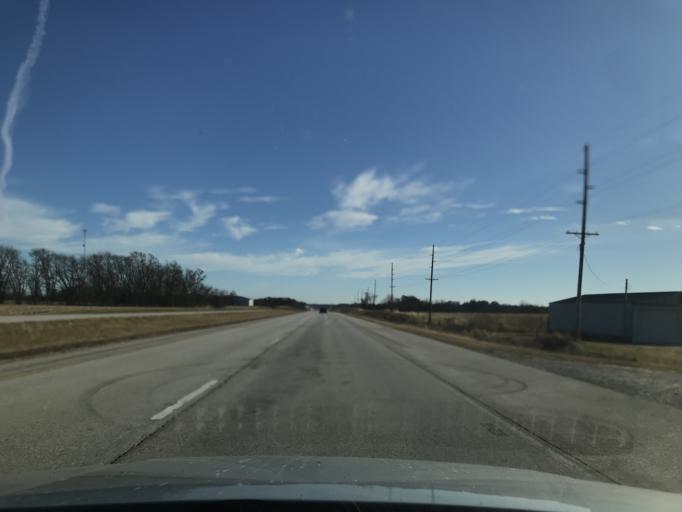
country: US
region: Illinois
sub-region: Hancock County
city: Carthage
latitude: 40.4148
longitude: -91.0429
